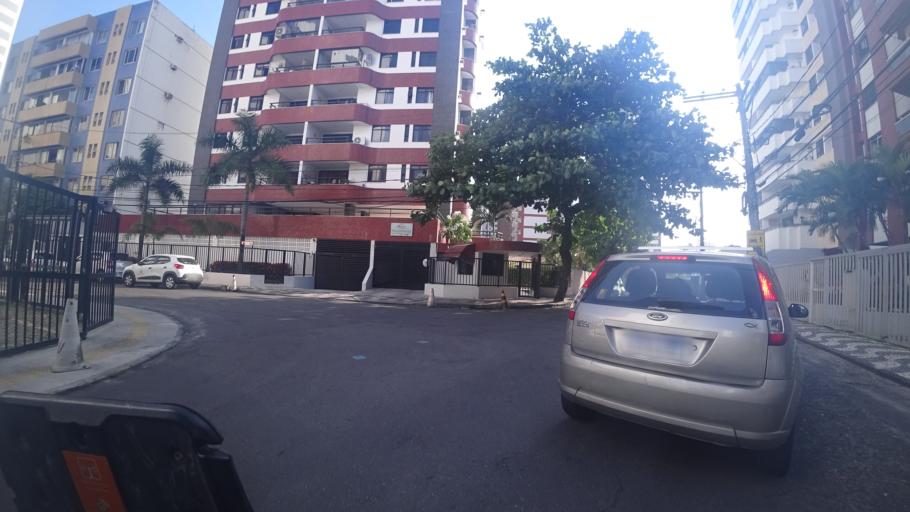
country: BR
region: Bahia
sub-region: Salvador
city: Salvador
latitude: -12.9973
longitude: -38.4528
